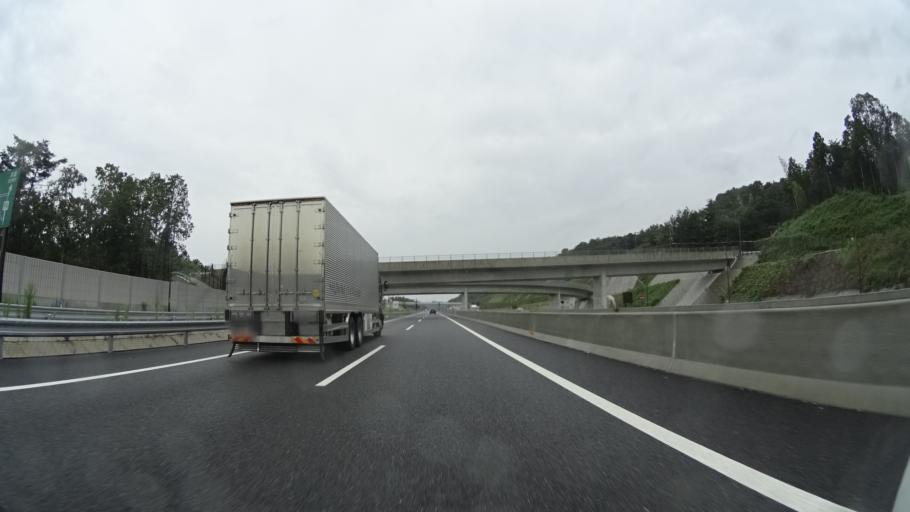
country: JP
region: Osaka
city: Ibaraki
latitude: 34.8857
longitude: 135.5362
